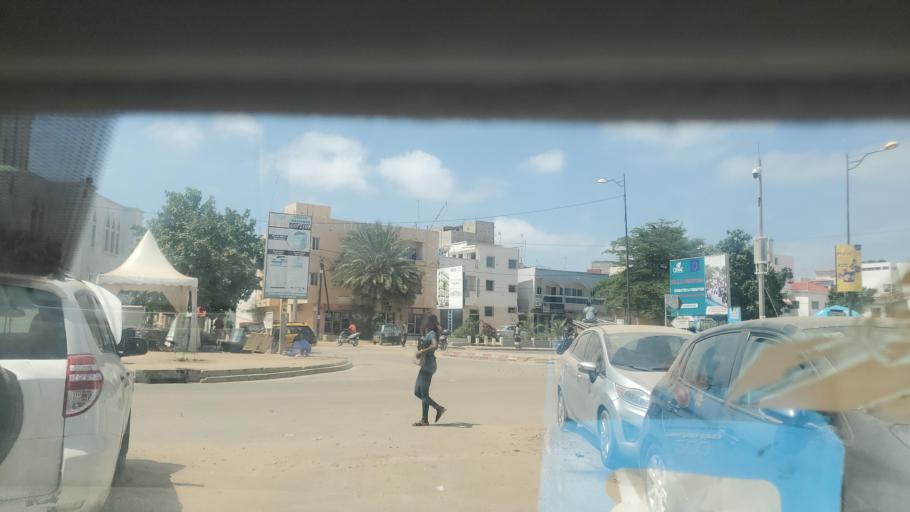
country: SN
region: Dakar
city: Grand Dakar
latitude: 14.7305
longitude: -17.4582
